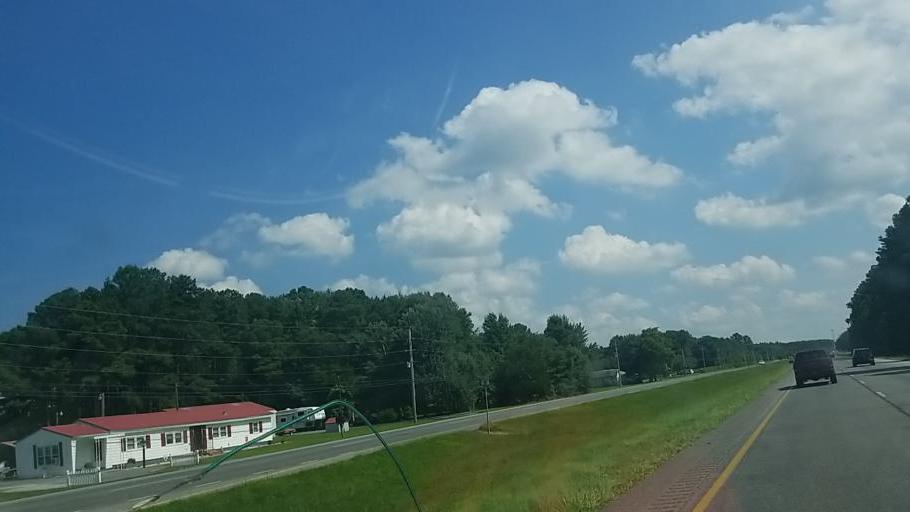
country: US
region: Delaware
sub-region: Sussex County
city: Georgetown
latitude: 38.7217
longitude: -75.4105
